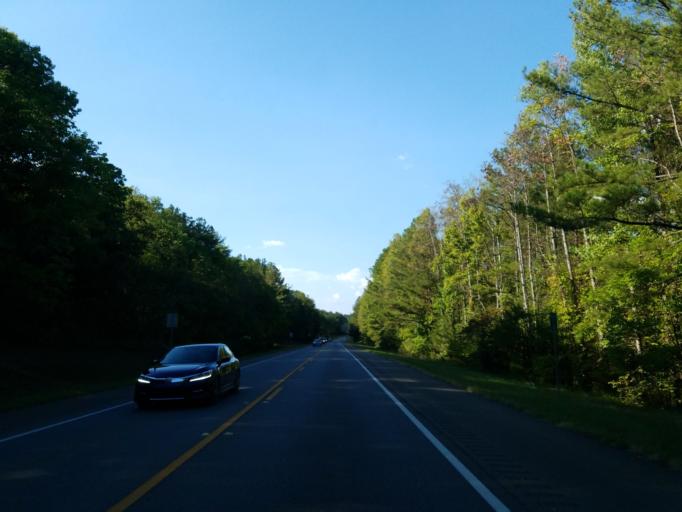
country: US
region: Georgia
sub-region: Murray County
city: Chatsworth
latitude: 34.5958
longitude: -84.7093
